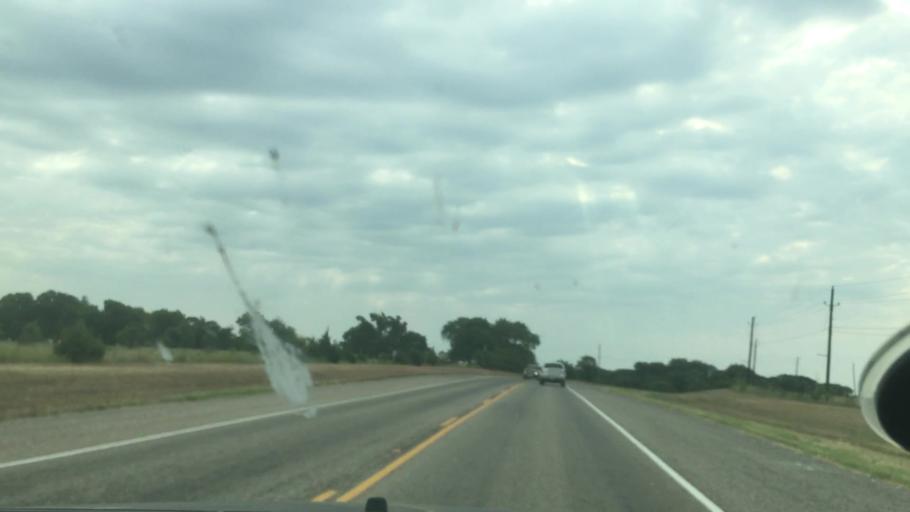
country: US
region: Texas
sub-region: Grayson County
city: Pottsboro
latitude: 33.8016
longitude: -96.6555
